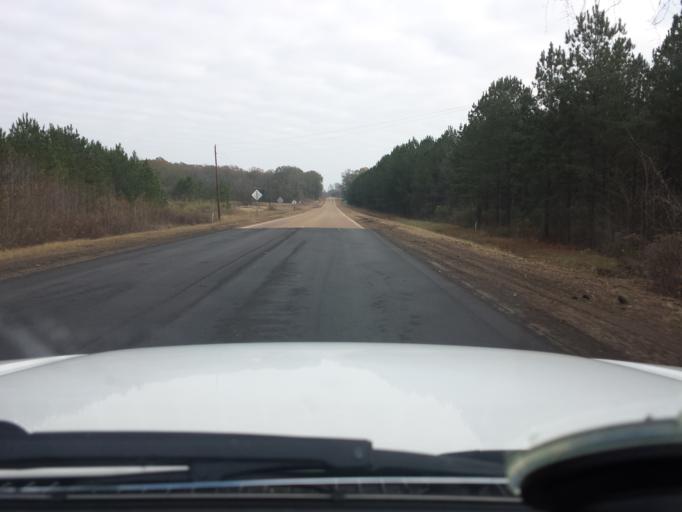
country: US
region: Mississippi
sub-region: Yazoo County
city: Yazoo City
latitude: 32.7943
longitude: -90.2108
